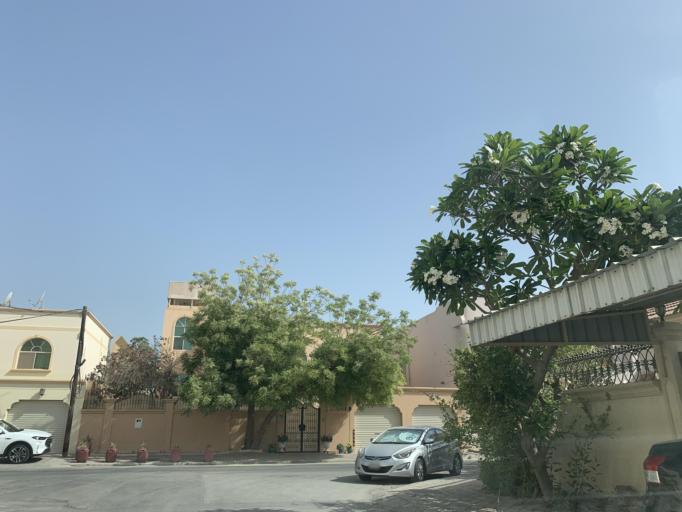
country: BH
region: Northern
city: Ar Rifa'
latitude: 26.1485
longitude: 50.5800
